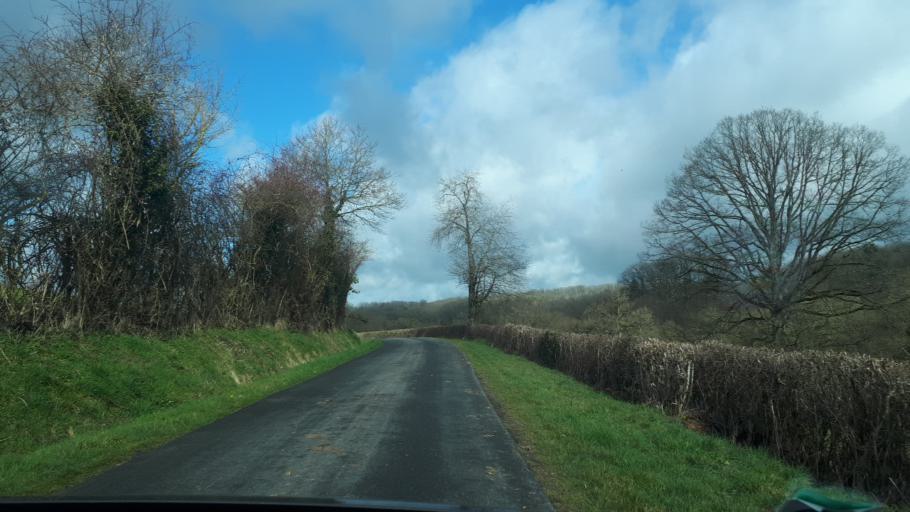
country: FR
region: Centre
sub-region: Departement du Loir-et-Cher
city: Sarge-sur-Braye
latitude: 47.9122
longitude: 0.8696
